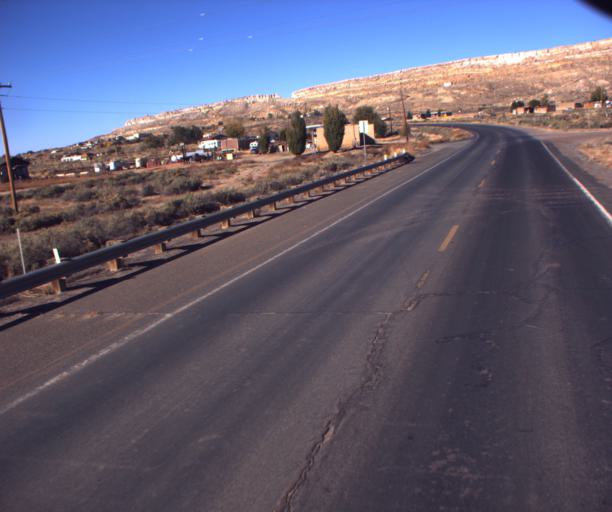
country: US
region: Arizona
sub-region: Navajo County
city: First Mesa
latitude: 35.8410
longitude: -110.3668
